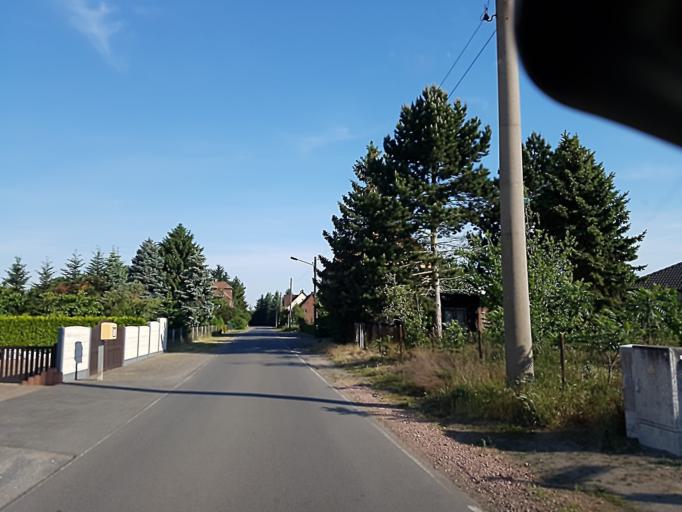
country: DE
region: Saxony-Anhalt
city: Abtsdorf
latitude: 51.8666
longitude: 12.7058
